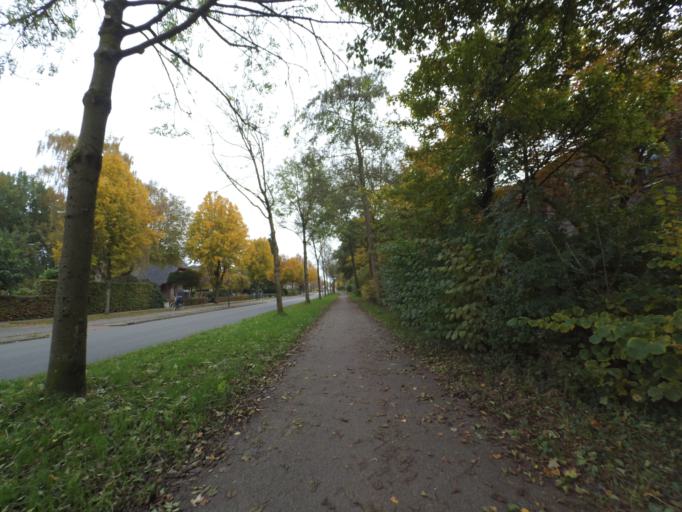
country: NL
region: Utrecht
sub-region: Gemeente Leusden
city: Leusden
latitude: 52.1375
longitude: 5.4210
